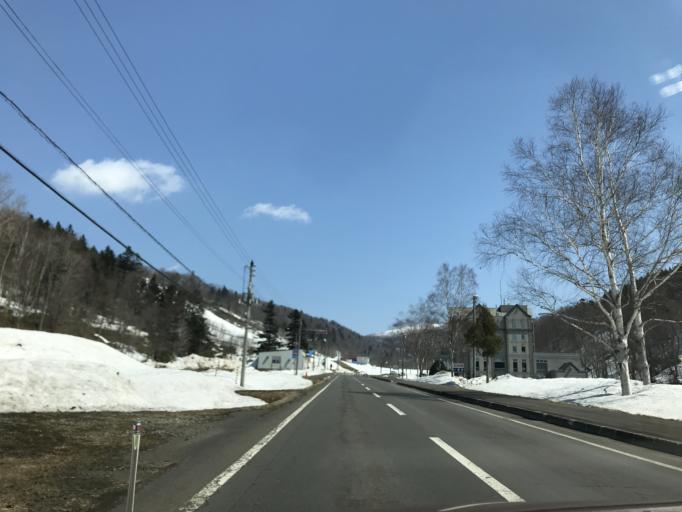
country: JP
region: Hokkaido
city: Nayoro
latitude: 44.4010
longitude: 142.5128
